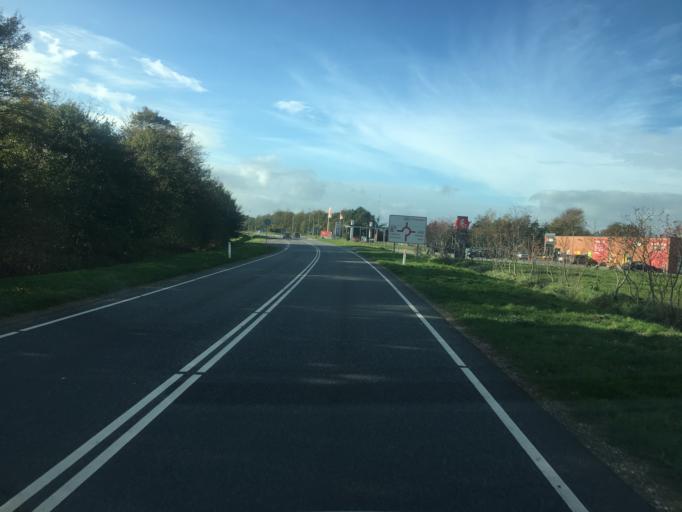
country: DK
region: South Denmark
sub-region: Tonder Kommune
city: Logumkloster
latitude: 55.0630
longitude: 8.9590
